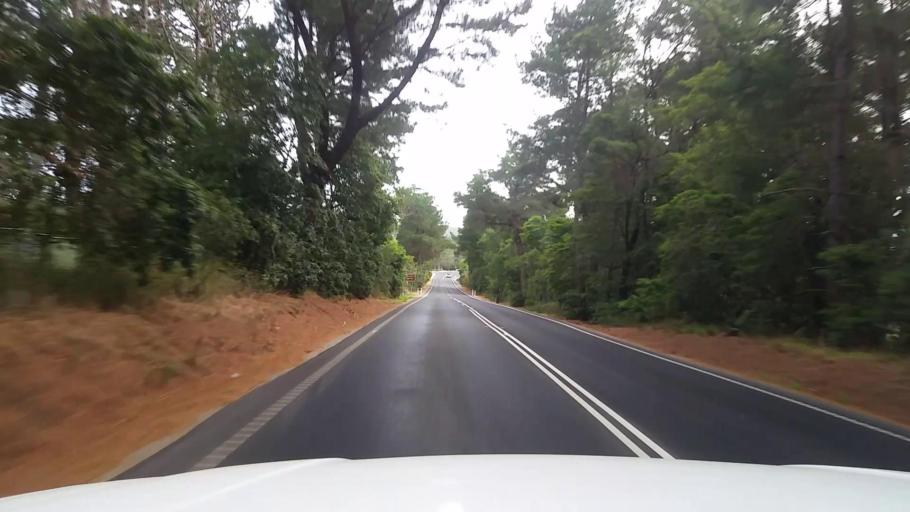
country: AU
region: Victoria
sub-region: Mornington Peninsula
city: Balnarring
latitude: -38.3563
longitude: 145.1098
